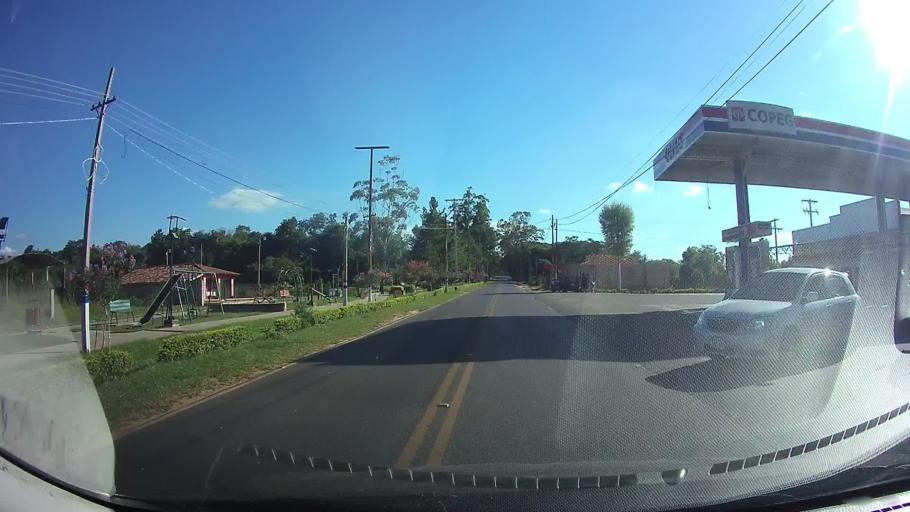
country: PY
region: Cordillera
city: Atyra
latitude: -25.2846
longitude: -57.1772
